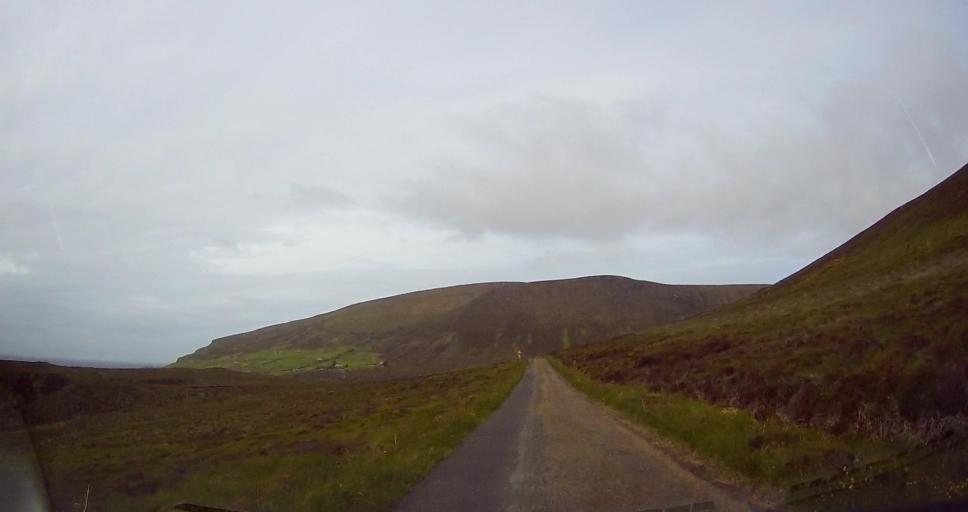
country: GB
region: Scotland
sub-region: Orkney Islands
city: Stromness
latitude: 58.8817
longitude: -3.3689
